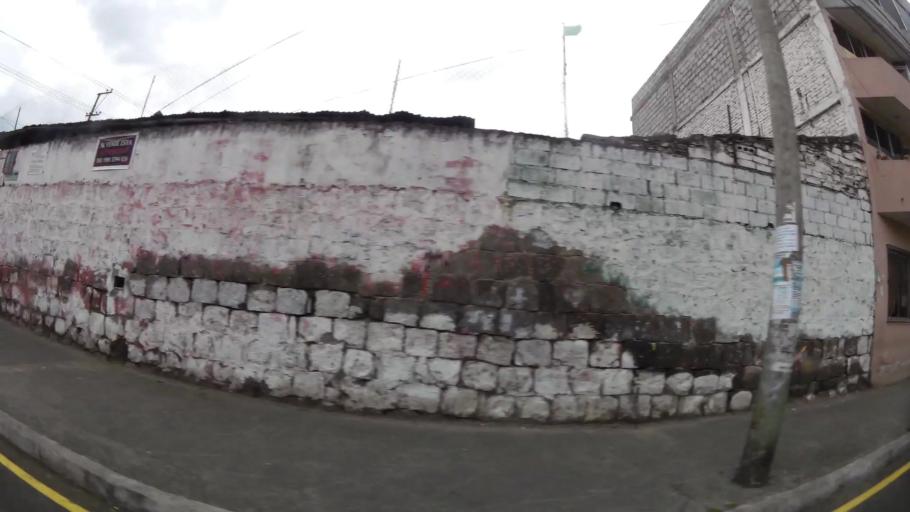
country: EC
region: Tungurahua
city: Ambato
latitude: -1.2306
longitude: -78.6189
